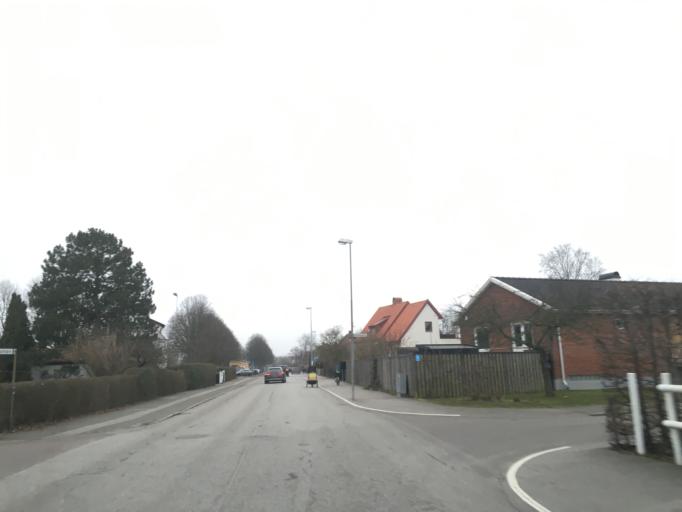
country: SE
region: Skane
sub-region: Lomma Kommun
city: Lomma
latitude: 55.6683
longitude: 13.0687
